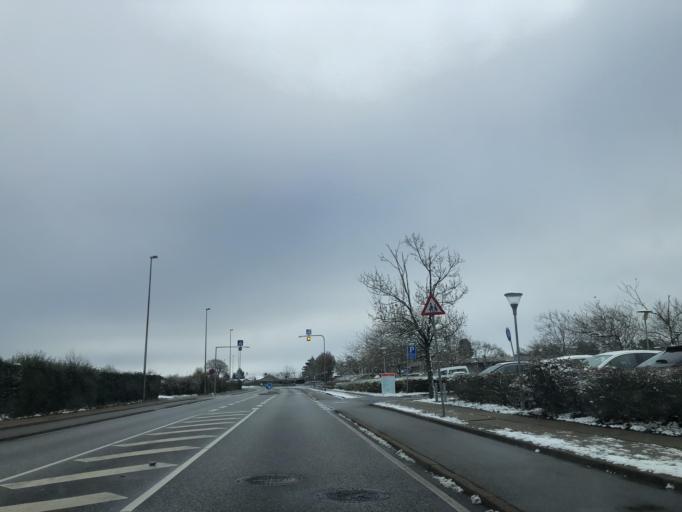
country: DK
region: Central Jutland
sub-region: Horsens Kommune
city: Horsens
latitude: 55.8366
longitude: 9.8339
